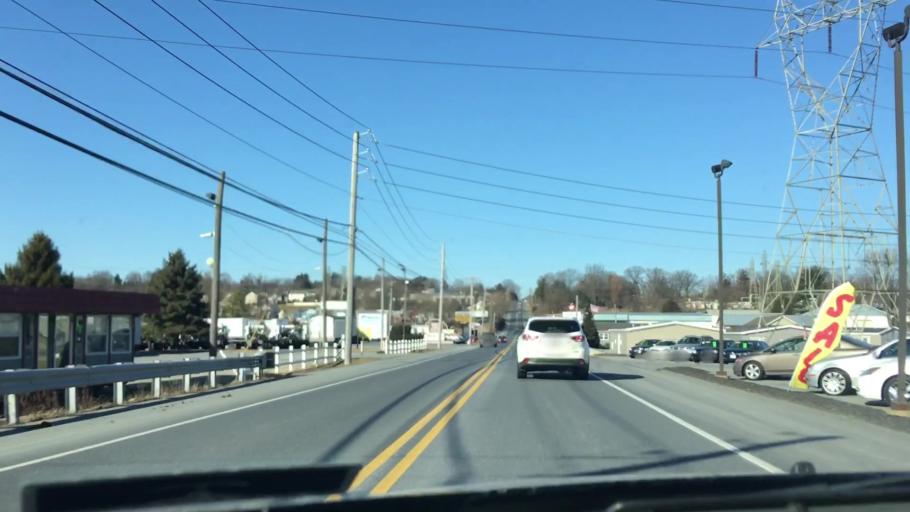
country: US
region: Pennsylvania
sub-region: Lancaster County
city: Brownstown
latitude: 40.1396
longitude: -76.2109
